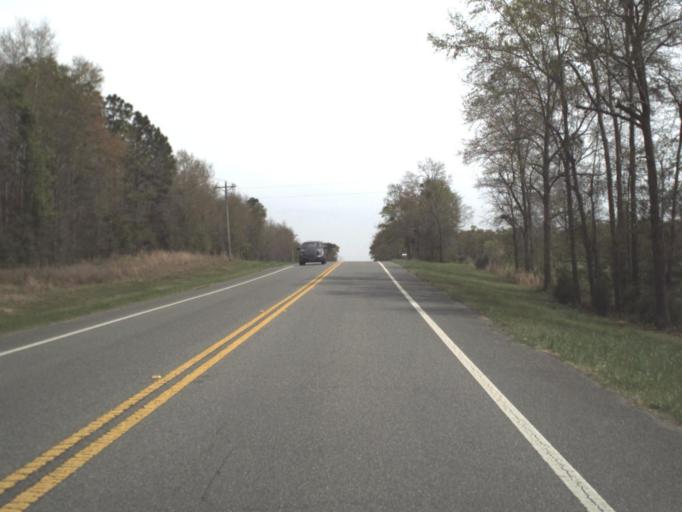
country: US
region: Alabama
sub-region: Geneva County
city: Geneva
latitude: 30.9573
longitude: -85.8962
